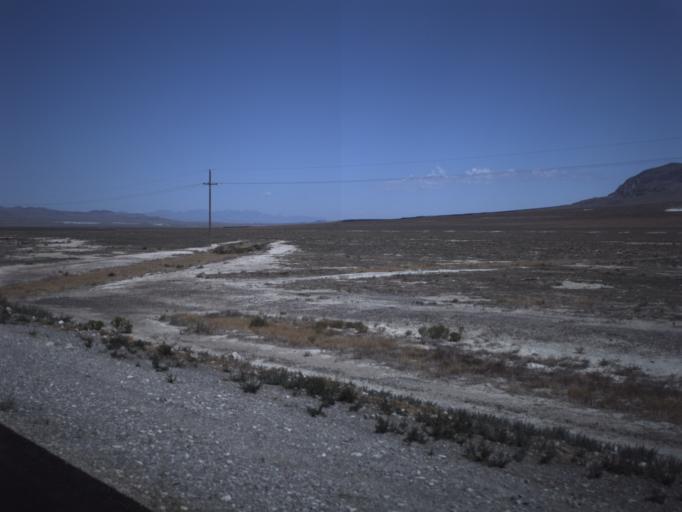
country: US
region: Utah
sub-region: Beaver County
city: Milford
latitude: 39.0628
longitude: -113.4425
